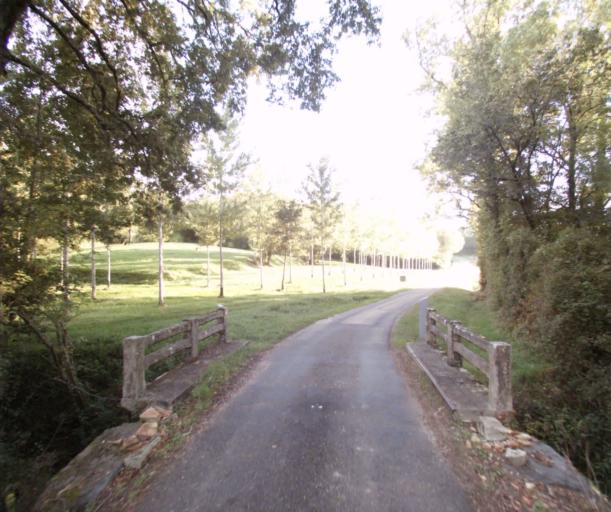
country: FR
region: Midi-Pyrenees
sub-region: Departement du Gers
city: Cazaubon
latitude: 43.8741
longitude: -0.0033
